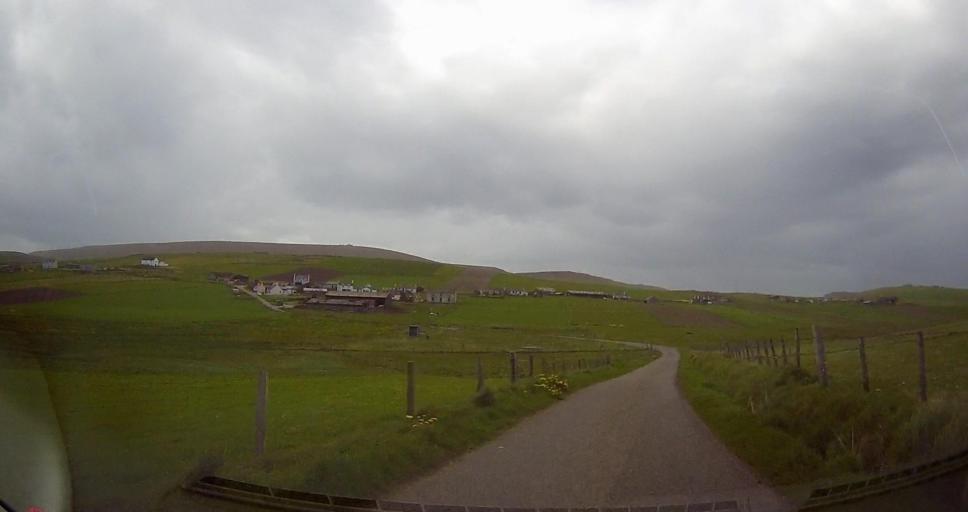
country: GB
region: Scotland
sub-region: Shetland Islands
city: Sandwick
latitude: 59.9113
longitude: -1.3282
